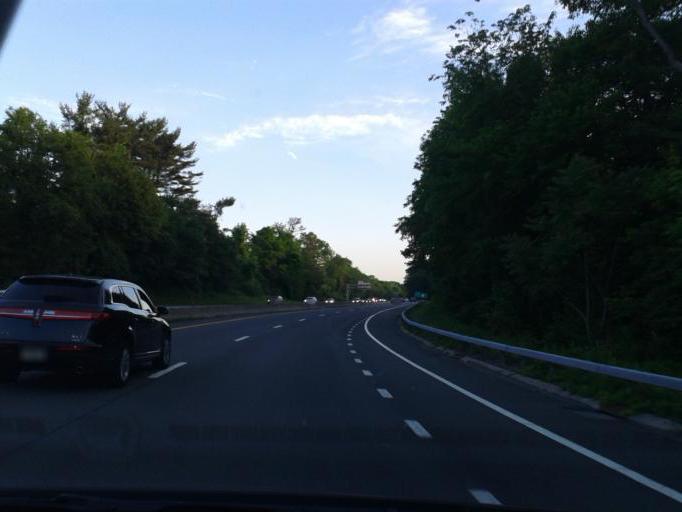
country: US
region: New York
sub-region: Westchester County
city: Tuckahoe
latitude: 40.9507
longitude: -73.7979
